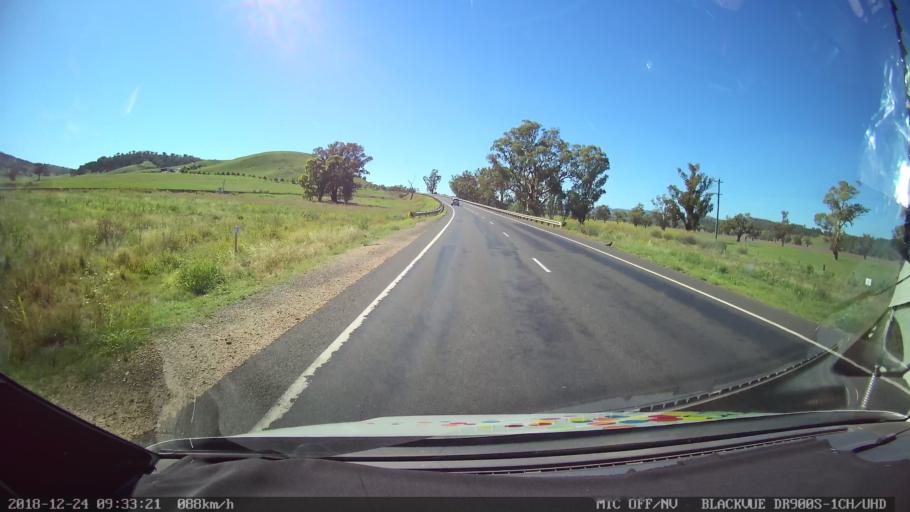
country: AU
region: New South Wales
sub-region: Liverpool Plains
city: Quirindi
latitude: -31.6025
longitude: 150.7067
